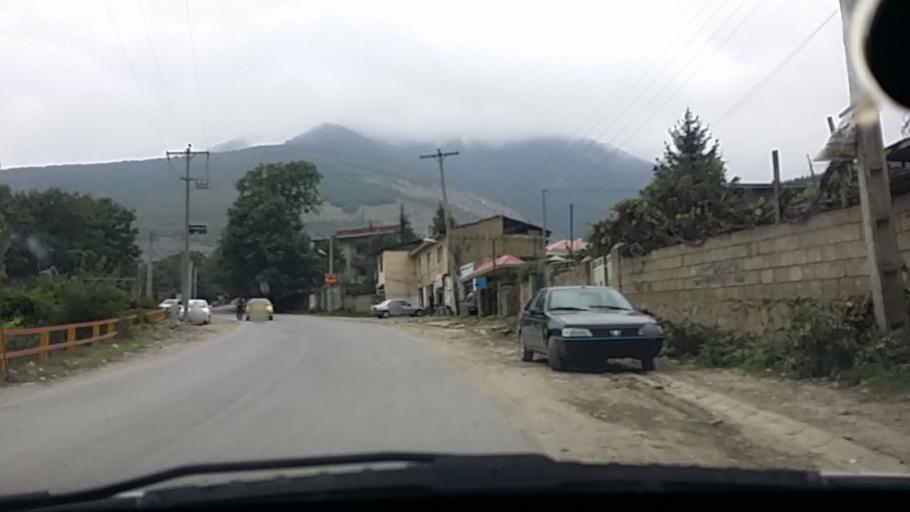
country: IR
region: Mazandaran
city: `Abbasabad
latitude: 36.4856
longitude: 51.1327
